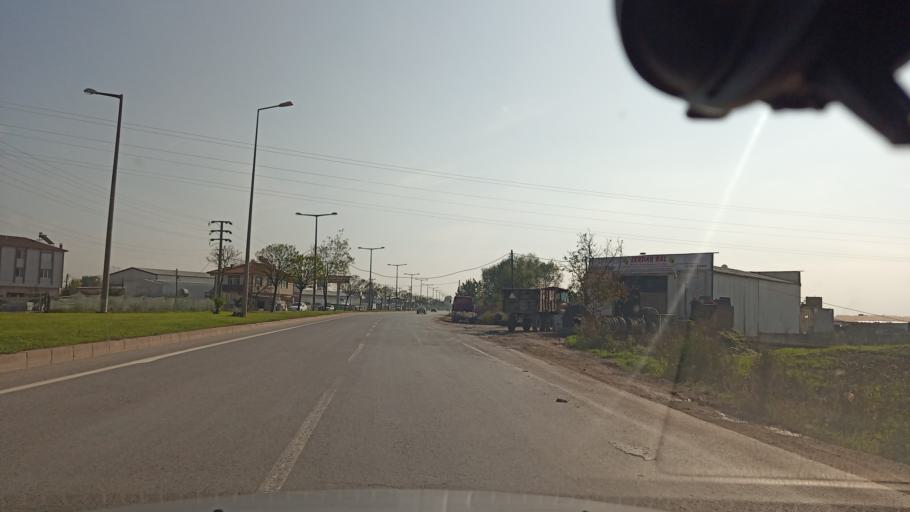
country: TR
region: Sakarya
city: Adapazari
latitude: 40.8212
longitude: 30.3973
